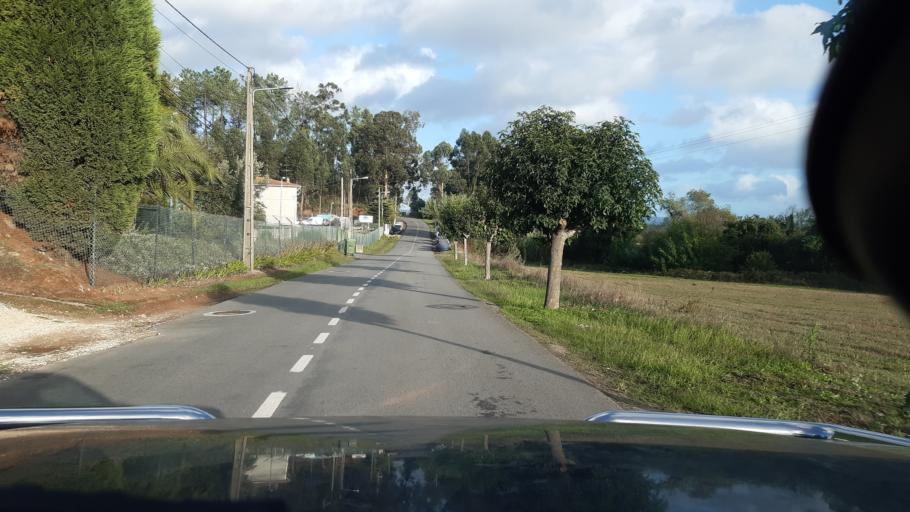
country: PT
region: Aveiro
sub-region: Agueda
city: Agueda
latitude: 40.5746
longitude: -8.4626
